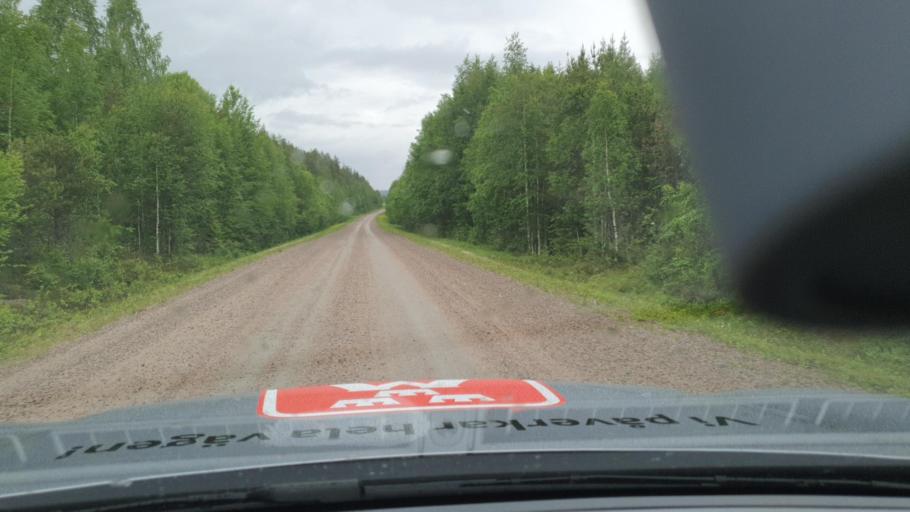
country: SE
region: Norrbotten
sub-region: Overkalix Kommun
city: OEverkalix
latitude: 66.5887
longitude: 22.7464
